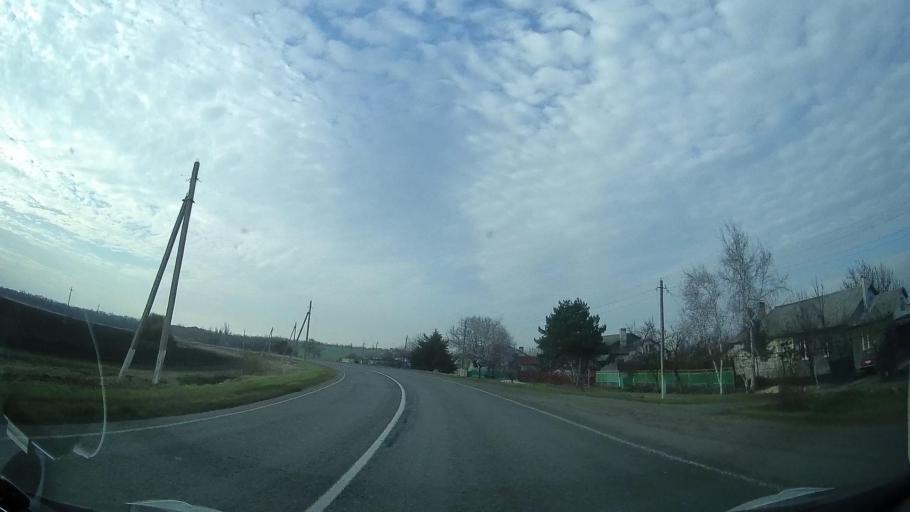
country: RU
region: Rostov
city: Bagayevskaya
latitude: 47.0955
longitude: 40.3128
